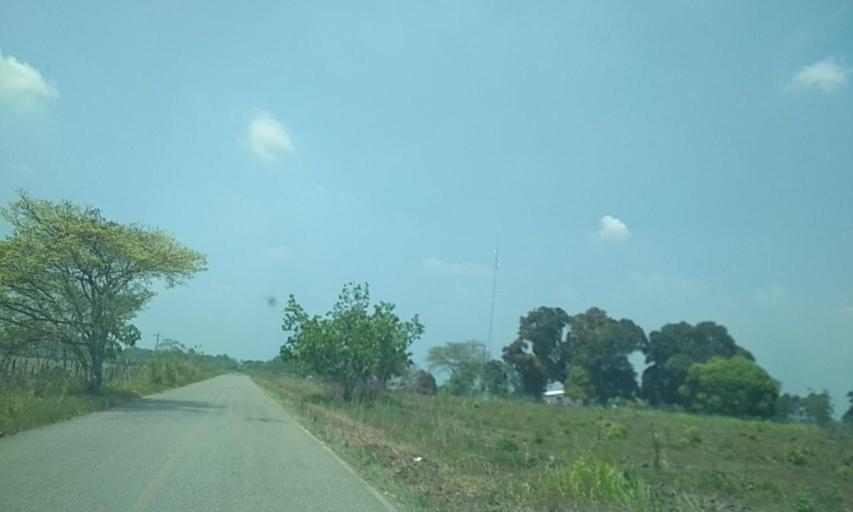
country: MX
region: Tabasco
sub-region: Huimanguillo
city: Paso de la Mina 3ra. Seccion
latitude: 17.8362
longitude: -93.6159
